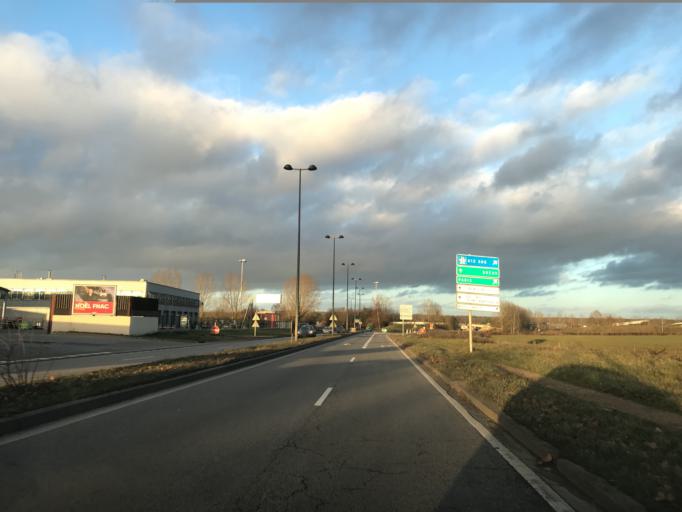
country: FR
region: Ile-de-France
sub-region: Departement des Yvelines
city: Elancourt
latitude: 48.7963
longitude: 1.9644
